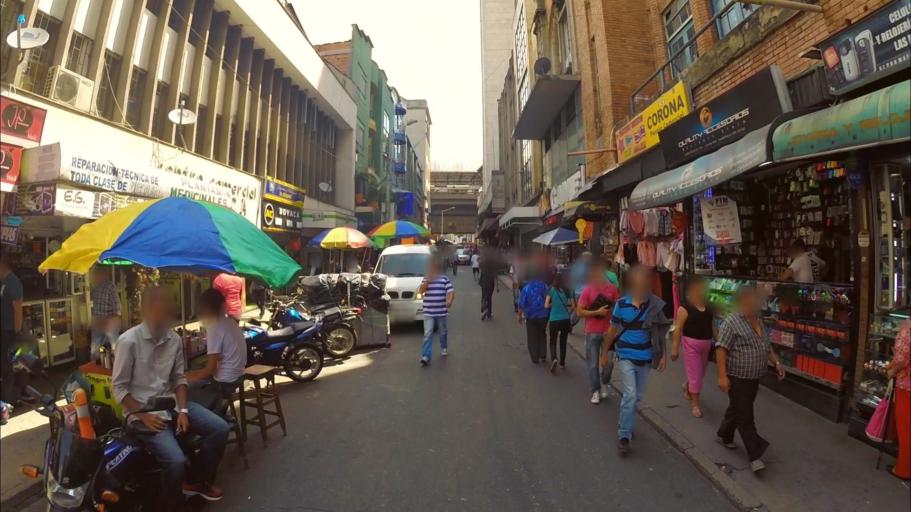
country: CO
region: Antioquia
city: Medellin
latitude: 6.2509
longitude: -75.5691
